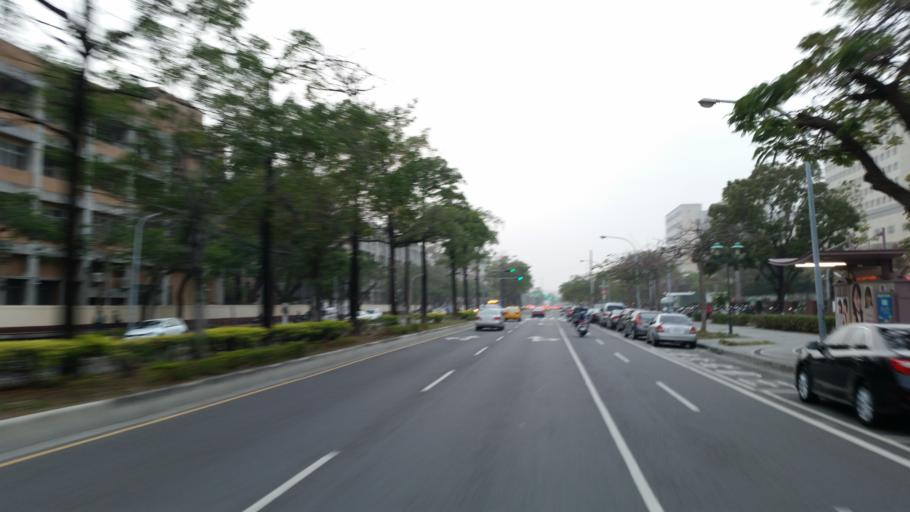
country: TW
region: Taiwan
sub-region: Tainan
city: Tainan
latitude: 23.0008
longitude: 120.2217
